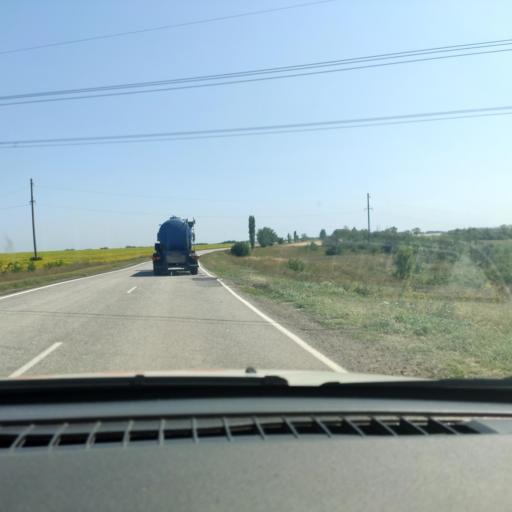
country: RU
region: Voronezj
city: Ostrogozhsk
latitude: 50.8126
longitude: 39.2721
